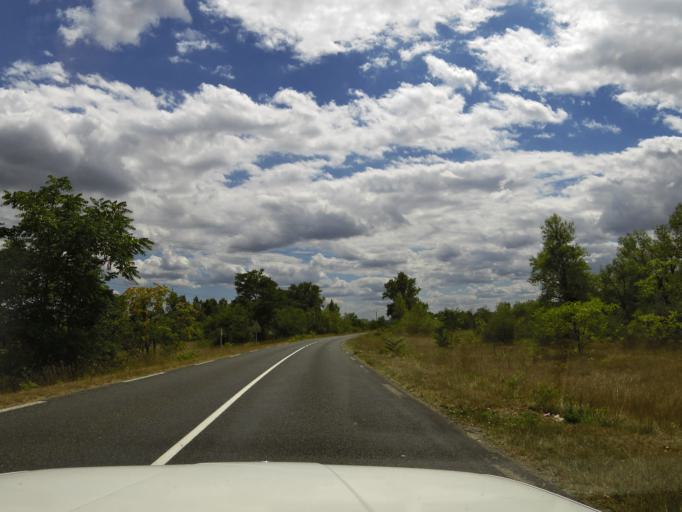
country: FR
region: Rhone-Alpes
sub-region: Departement de l'Ain
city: Saint-Jean-de-Niost
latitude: 45.8133
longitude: 5.2150
